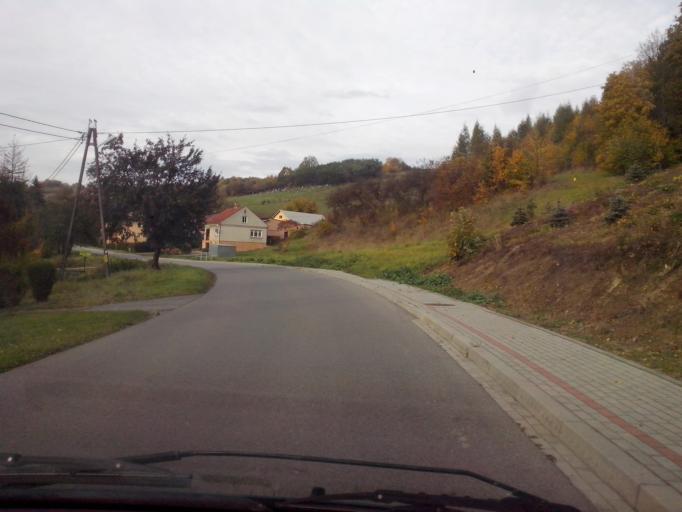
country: PL
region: Subcarpathian Voivodeship
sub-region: Powiat strzyzowski
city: Wisniowa
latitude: 49.8859
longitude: 21.6701
